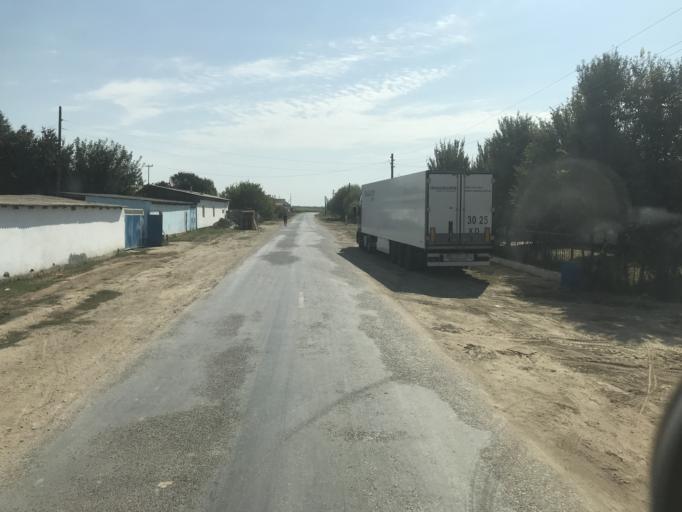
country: KZ
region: Ongtustik Qazaqstan
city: Myrzakent
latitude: 40.6641
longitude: 68.6293
